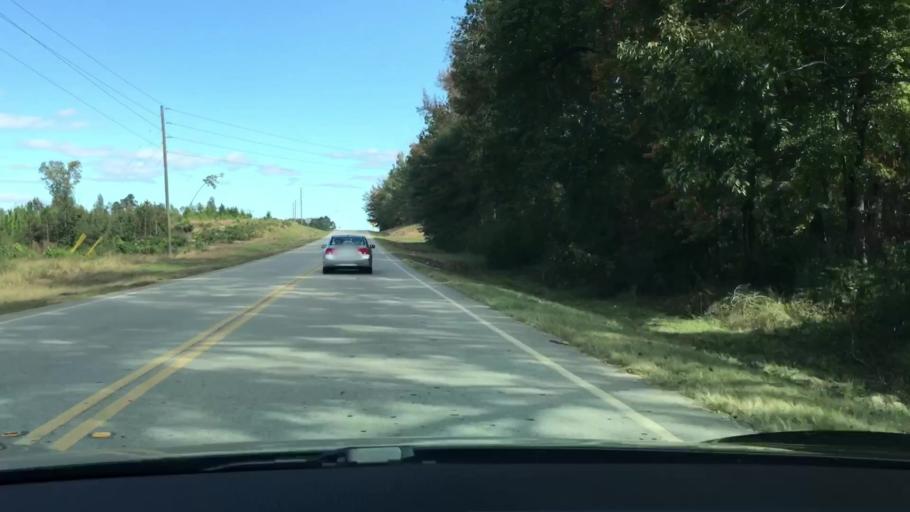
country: US
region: Georgia
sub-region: Jefferson County
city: Wrens
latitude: 33.2249
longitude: -82.4619
